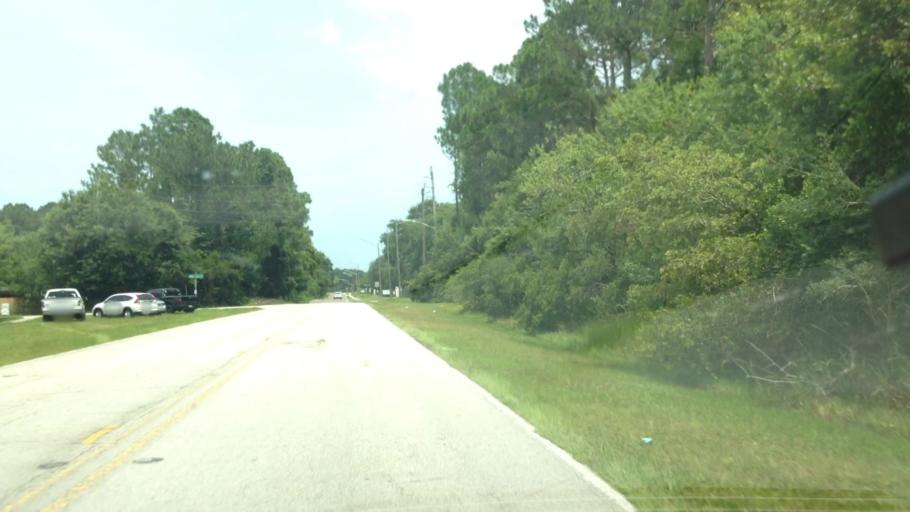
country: US
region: Florida
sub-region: Duval County
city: Neptune Beach
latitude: 30.3018
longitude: -81.5108
